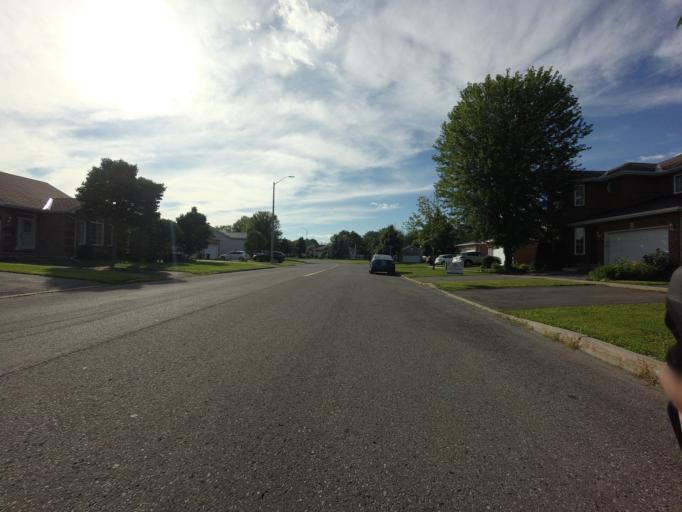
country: CA
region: Ontario
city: Ottawa
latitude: 45.2875
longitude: -75.6854
